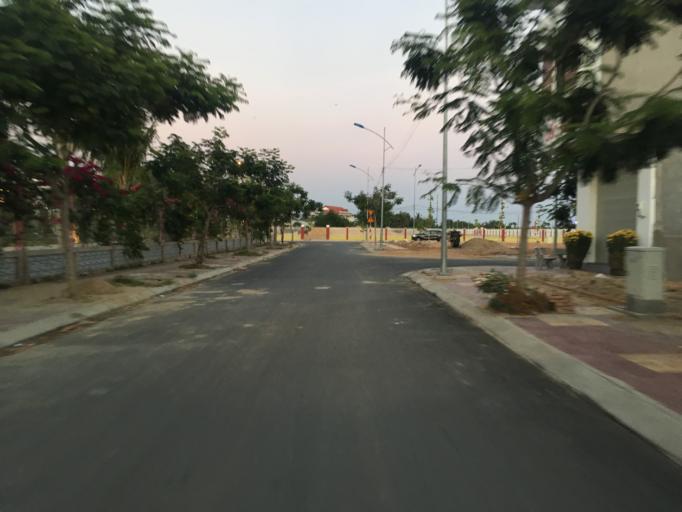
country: VN
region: Ninh Thuan
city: Phan Rang-Thap Cham
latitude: 11.5771
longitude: 108.9969
